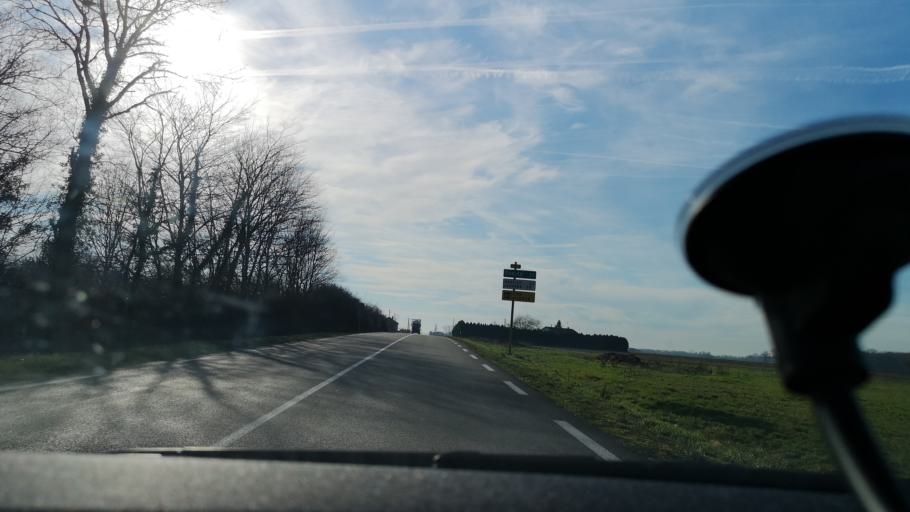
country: FR
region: Bourgogne
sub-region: Departement de la Cote-d'Or
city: Seurre
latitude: 46.9624
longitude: 5.1722
